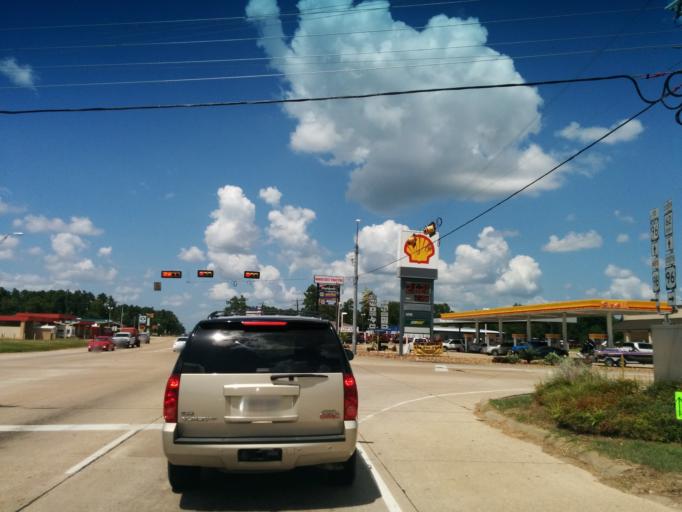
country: US
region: Texas
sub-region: Jasper County
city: Buna
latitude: 30.4413
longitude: -93.9693
